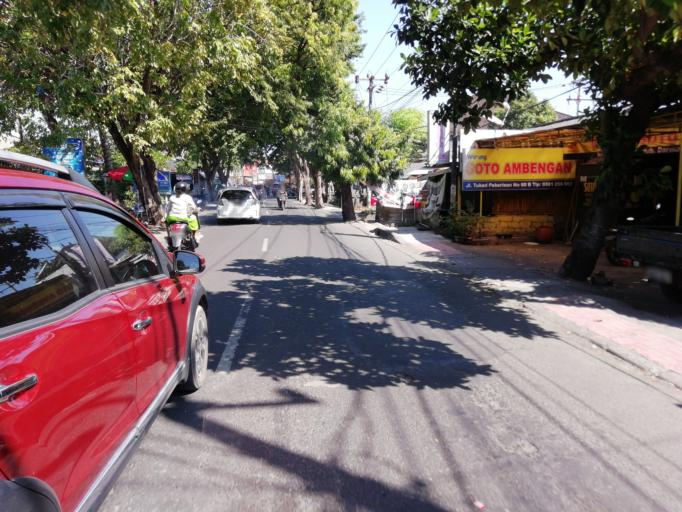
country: ID
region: Bali
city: Karyadharma
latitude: -8.6890
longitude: 115.2263
